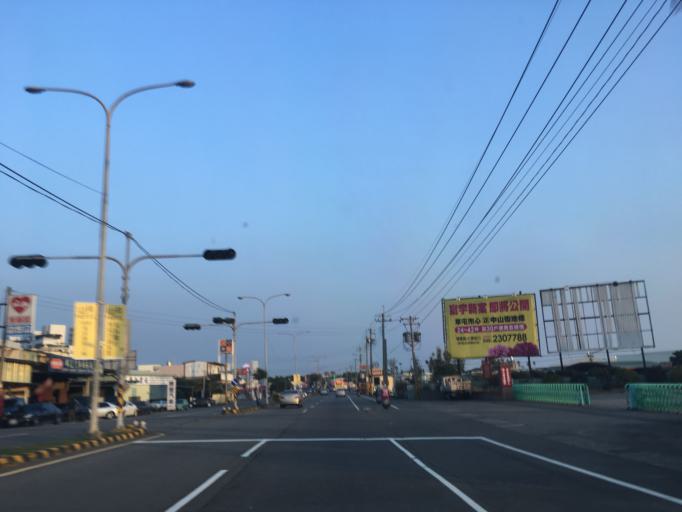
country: TW
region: Taiwan
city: Zhongxing New Village
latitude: 23.9950
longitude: 120.6654
